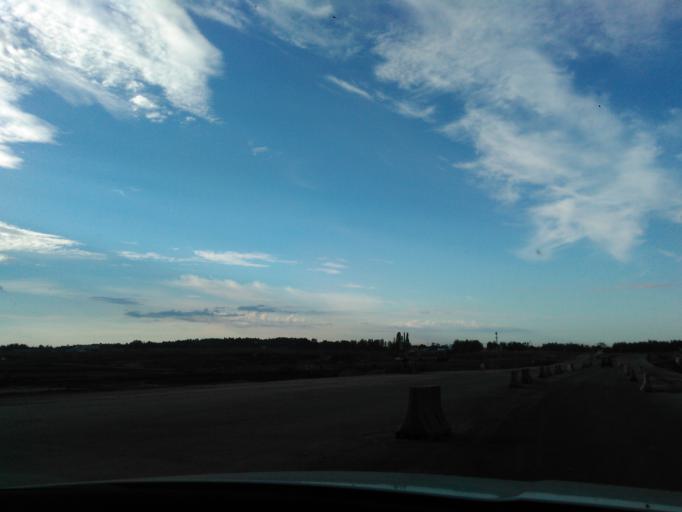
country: RU
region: Moskovskaya
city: Lobnya
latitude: 55.9810
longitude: 37.4530
